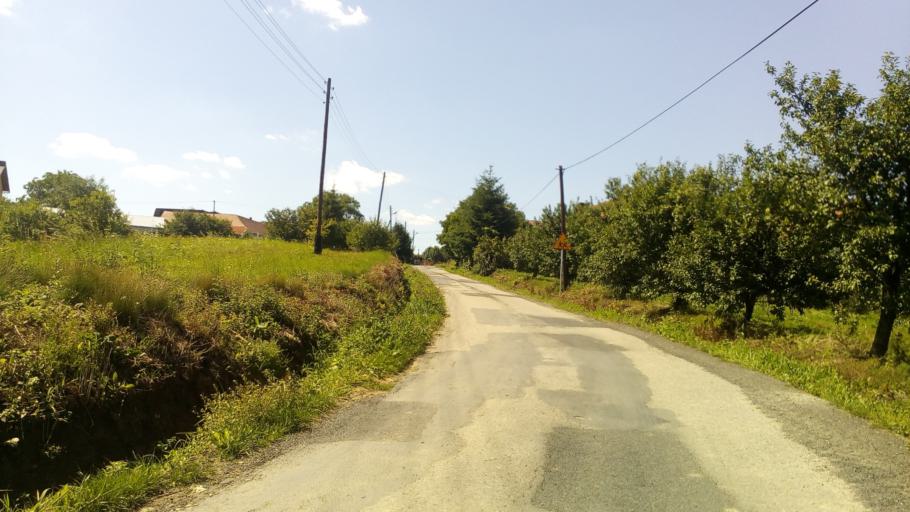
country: PL
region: Lesser Poland Voivodeship
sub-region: Powiat nowosadecki
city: Olszana
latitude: 49.5646
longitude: 20.4988
